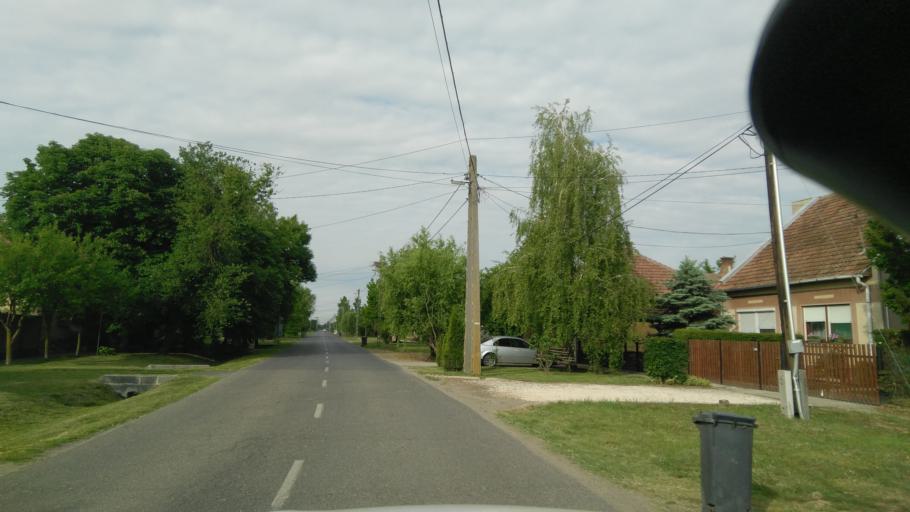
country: HU
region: Bekes
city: Ketegyhaza
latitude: 46.5491
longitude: 21.1828
